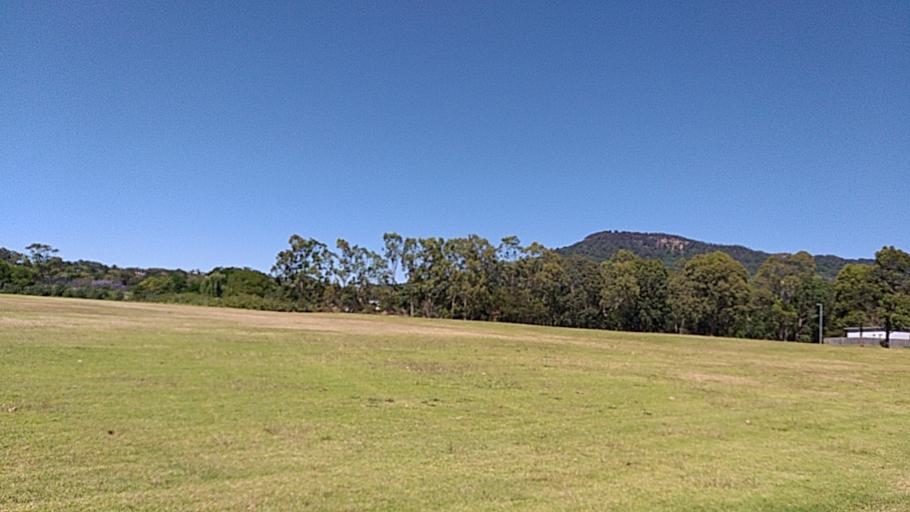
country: AU
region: New South Wales
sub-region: Wollongong
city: Fairy Meadow
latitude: -34.3915
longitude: 150.8902
